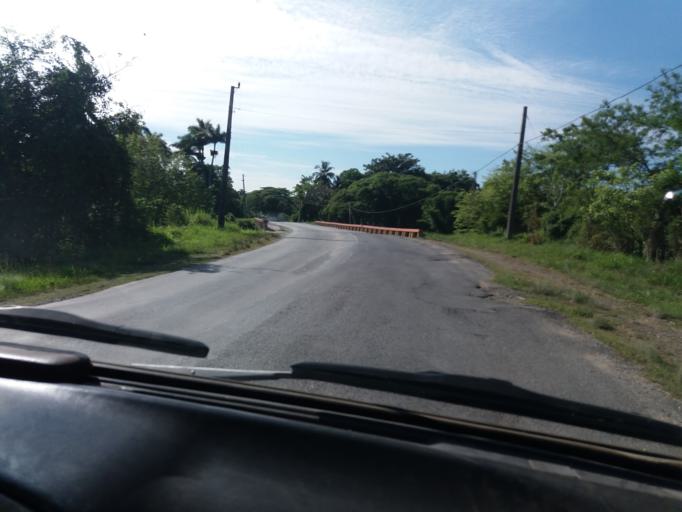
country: CU
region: Cienfuegos
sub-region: Municipio de Cienfuegos
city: Cienfuegos
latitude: 22.1639
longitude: -80.3676
